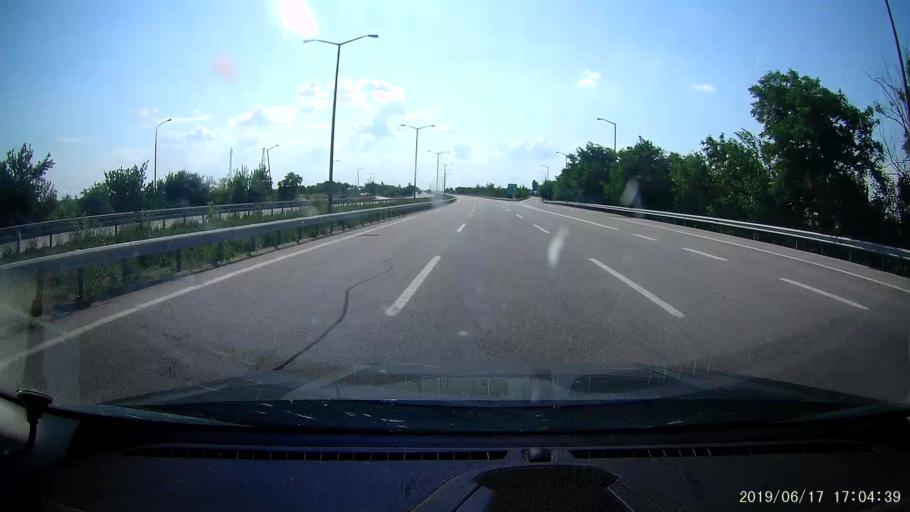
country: TR
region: Edirne
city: Haskoy
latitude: 41.6565
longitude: 26.7213
